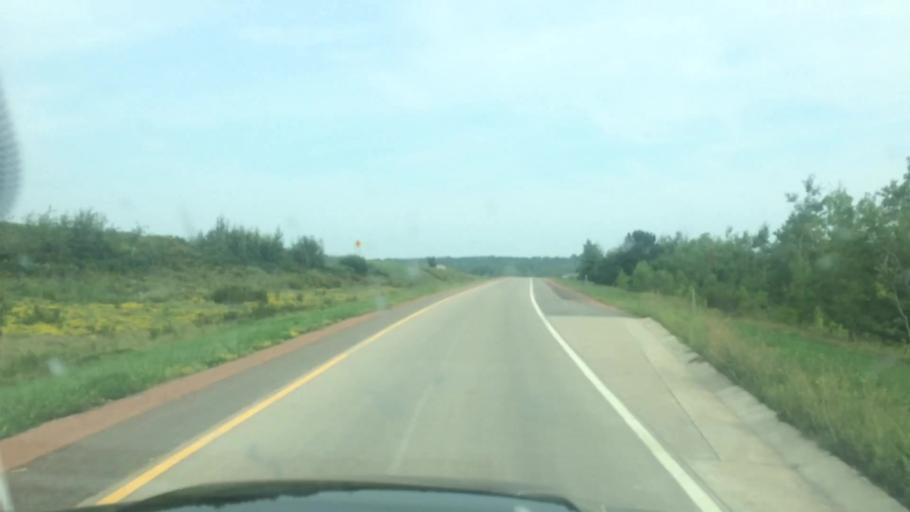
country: US
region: Wisconsin
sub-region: Marathon County
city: Wausau
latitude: 44.9902
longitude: -89.6556
